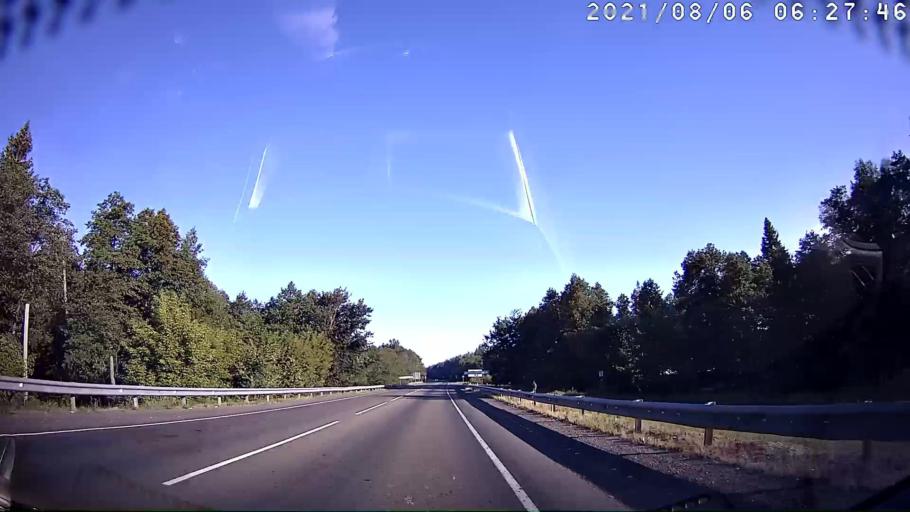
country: RU
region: Mariy-El
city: Krasnogorskiy
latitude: 56.1381
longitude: 48.3241
